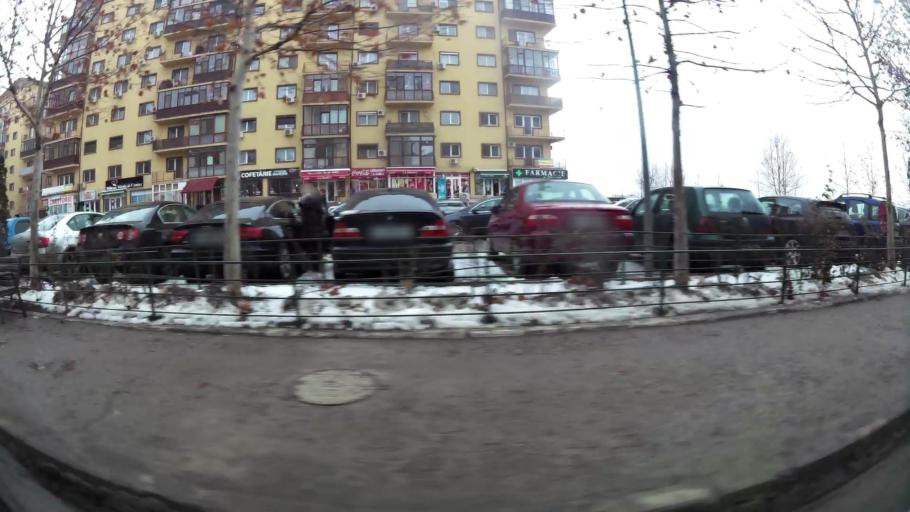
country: RO
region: Ilfov
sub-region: Comuna Chiajna
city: Chiajna
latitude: 44.4423
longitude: 25.9873
